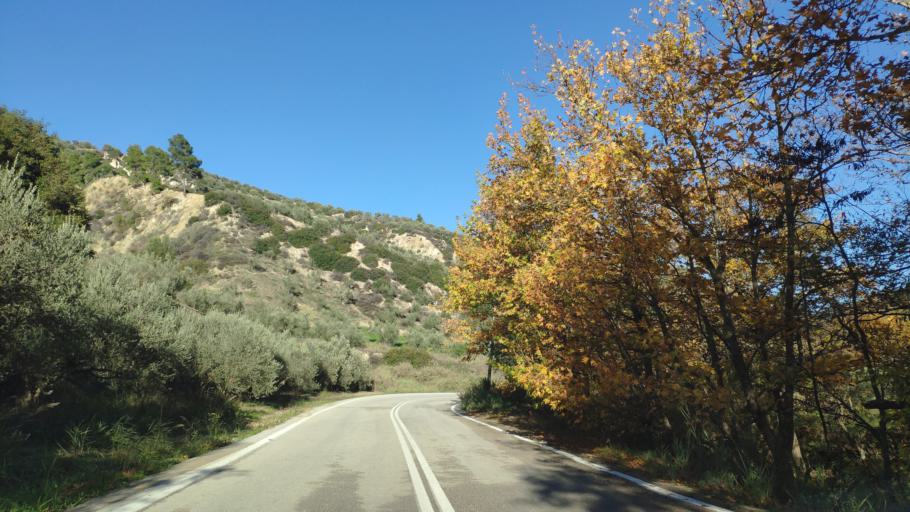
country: GR
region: Peloponnese
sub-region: Nomos Korinthias
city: Xylokastro
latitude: 38.0099
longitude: 22.5388
